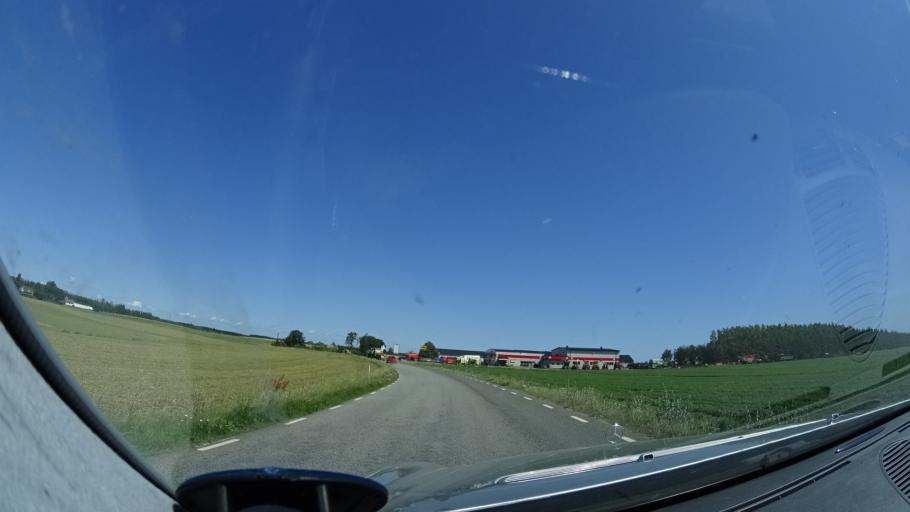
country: SE
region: Skane
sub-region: Kristianstads Kommun
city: Degeberga
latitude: 55.8910
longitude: 14.0387
